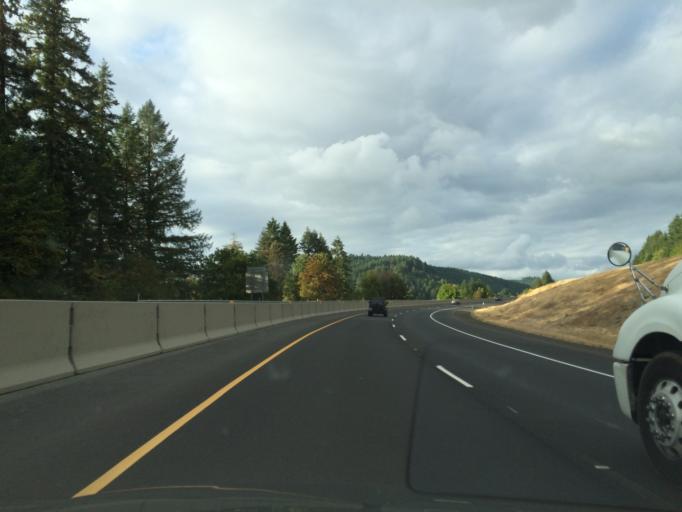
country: US
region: Oregon
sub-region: Douglas County
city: Drain
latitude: 43.7110
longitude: -123.2184
